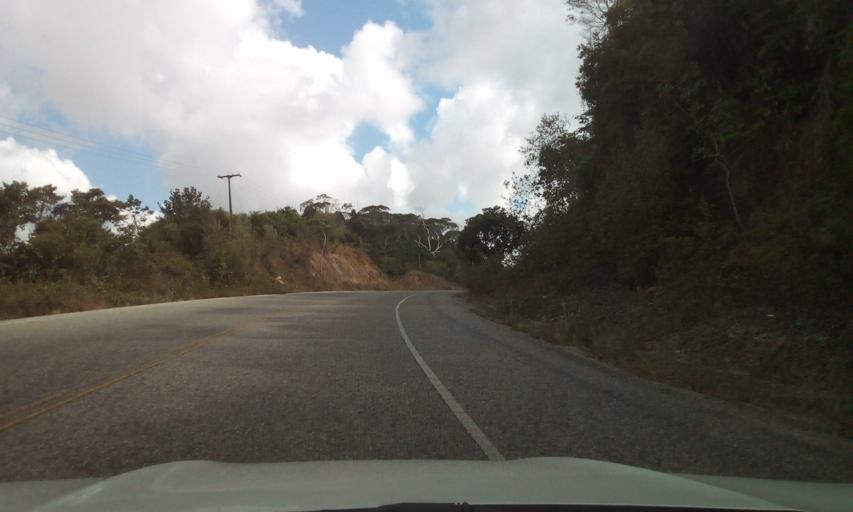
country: BR
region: Sergipe
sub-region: Indiaroba
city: Indiaroba
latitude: -11.4277
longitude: -37.4973
